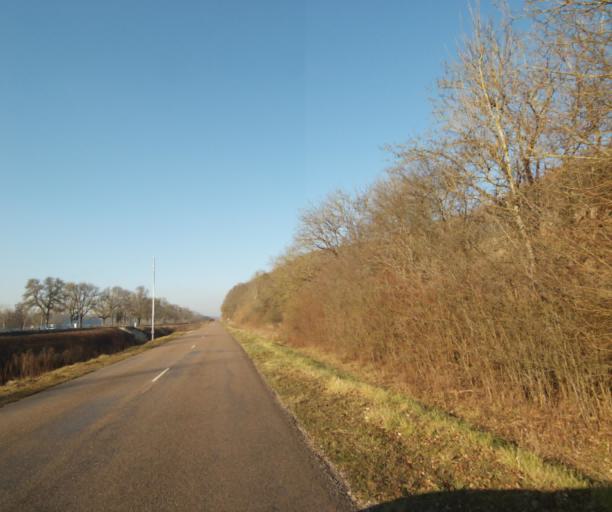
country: FR
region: Champagne-Ardenne
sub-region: Departement de la Haute-Marne
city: Chevillon
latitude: 48.5060
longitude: 5.1251
